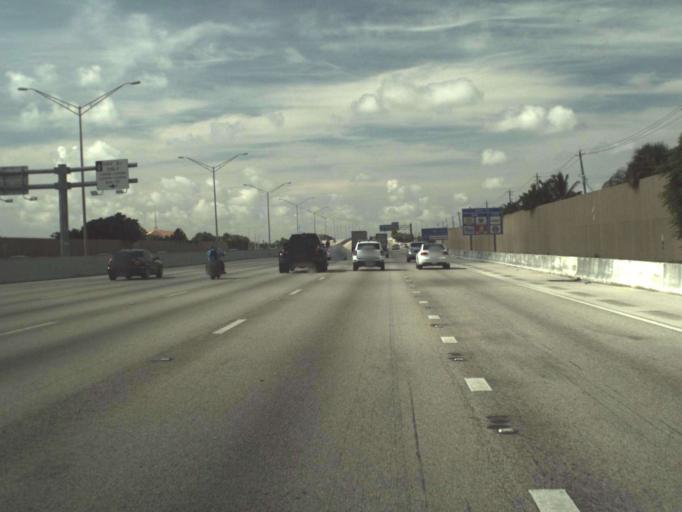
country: US
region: Florida
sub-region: Palm Beach County
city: North Palm Beach
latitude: 26.8161
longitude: -80.0982
